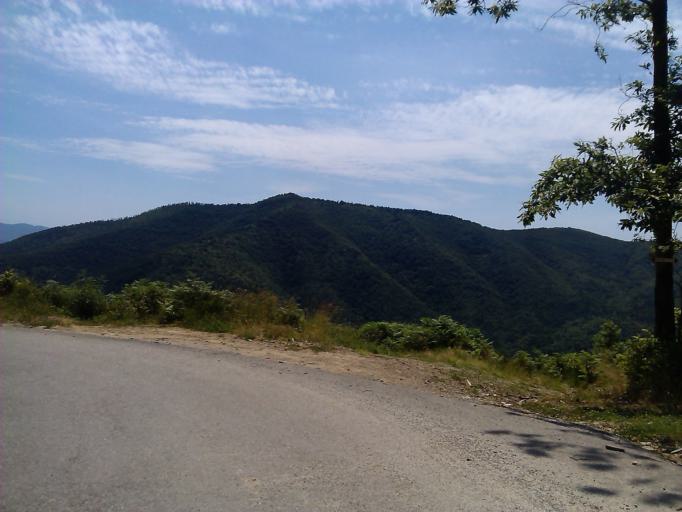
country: IT
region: Tuscany
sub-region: Provincia di Pistoia
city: Montale
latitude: 43.9755
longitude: 11.0373
